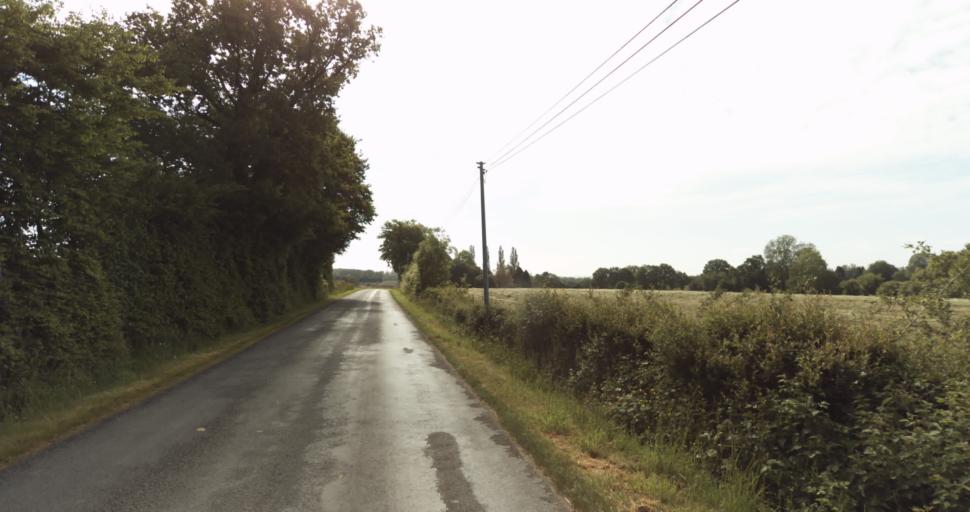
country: FR
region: Limousin
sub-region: Departement de la Haute-Vienne
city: Bosmie-l'Aiguille
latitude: 45.7096
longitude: 1.2359
